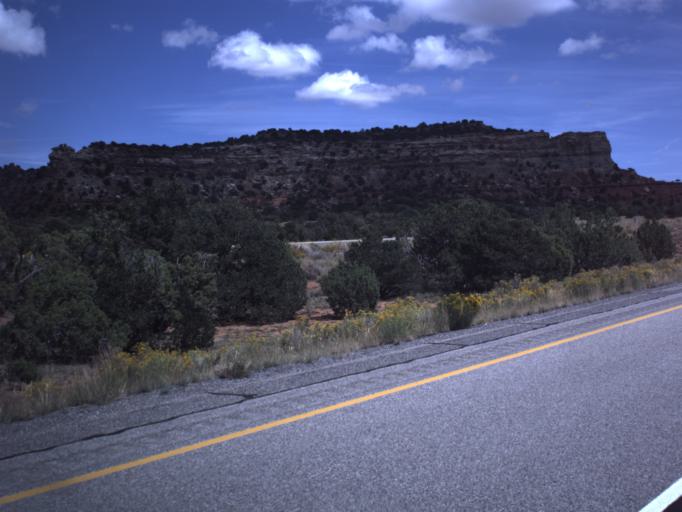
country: US
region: Utah
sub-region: Emery County
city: Castle Dale
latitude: 38.8692
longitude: -110.7223
